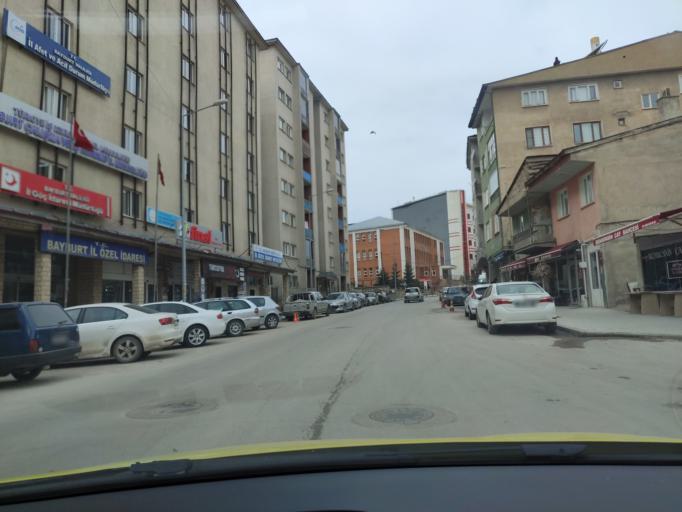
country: TR
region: Bayburt
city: Bayburt
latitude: 40.2534
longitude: 40.2256
